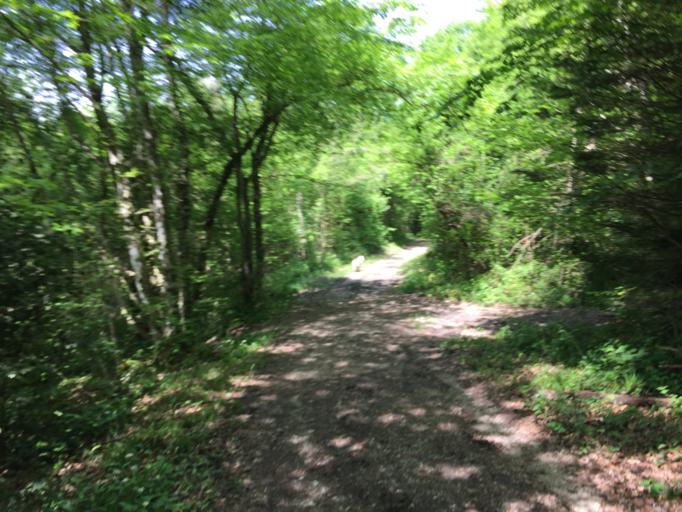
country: FR
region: Rhone-Alpes
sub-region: Departement de la Savoie
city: Mery
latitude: 45.6583
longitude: 5.9513
